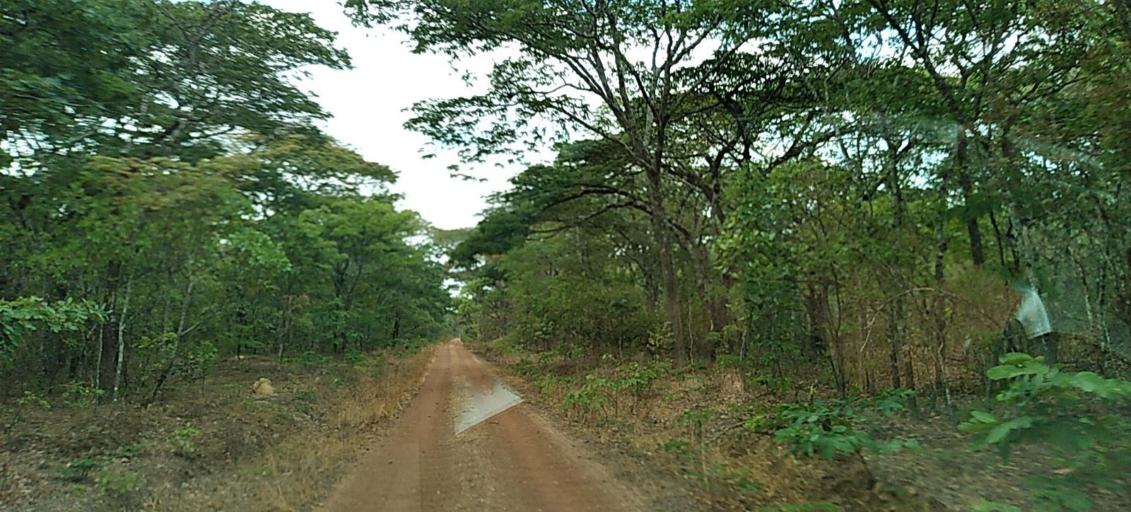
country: ZM
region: Copperbelt
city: Chililabombwe
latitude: -12.4582
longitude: 27.6002
